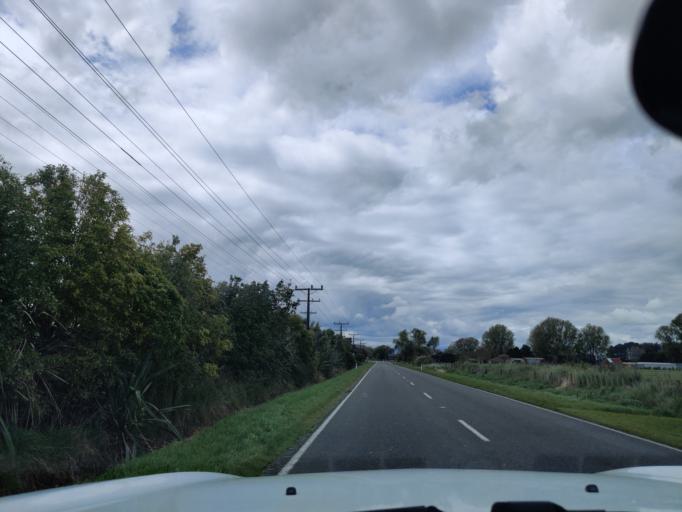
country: NZ
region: Manawatu-Wanganui
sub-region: Palmerston North City
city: Palmerston North
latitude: -40.2448
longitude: 175.5508
